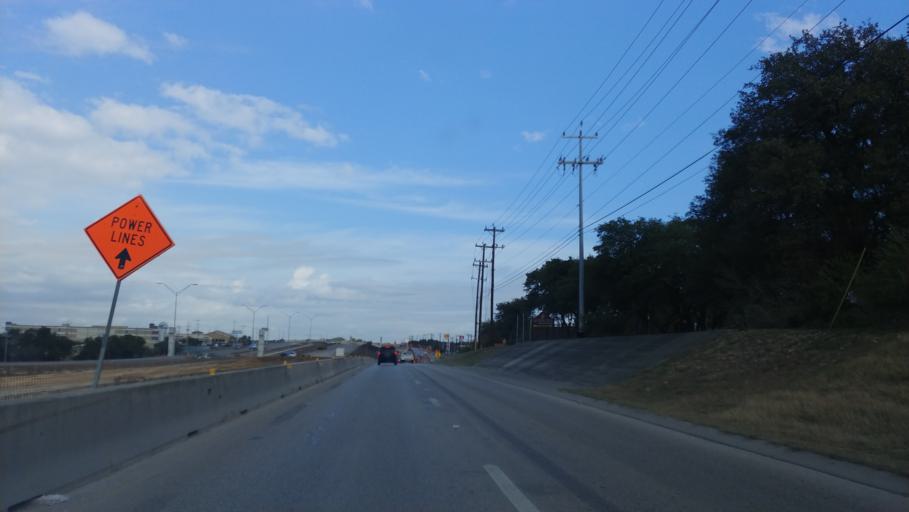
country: US
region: Texas
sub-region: Bexar County
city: Leon Valley
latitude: 29.4431
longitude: -98.7110
